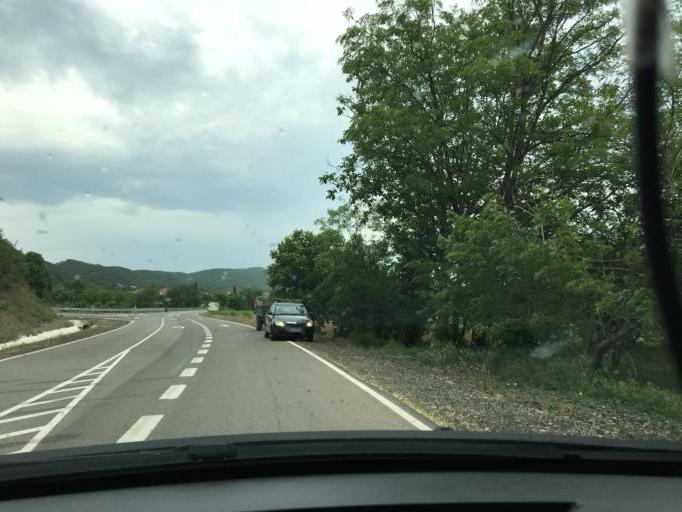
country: MK
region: Gevgelija
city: Miravci
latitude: 41.3035
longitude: 22.4447
